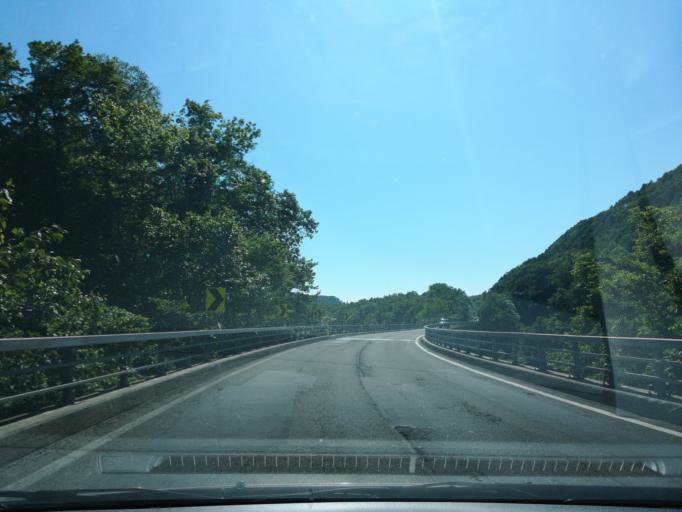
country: JP
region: Hokkaido
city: Chitose
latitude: 42.9104
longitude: 141.9452
